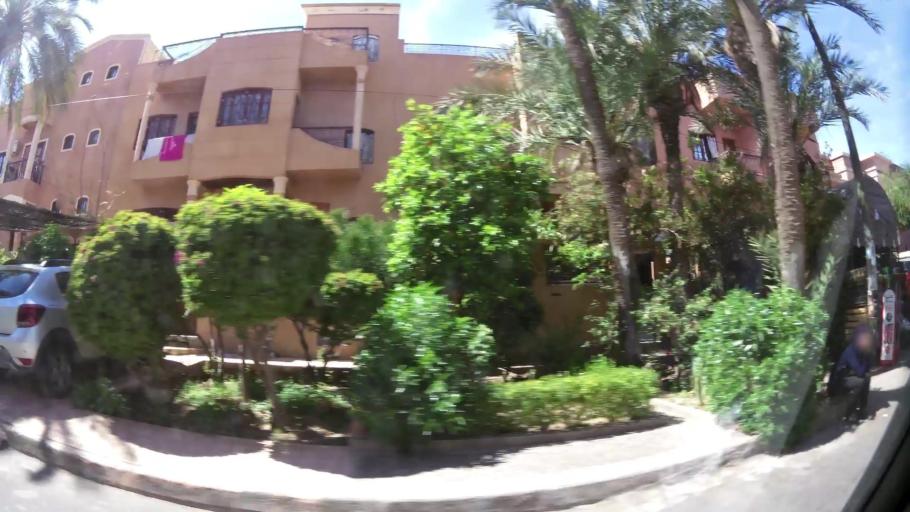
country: MA
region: Marrakech-Tensift-Al Haouz
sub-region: Marrakech
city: Marrakesh
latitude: 31.6739
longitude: -8.0021
